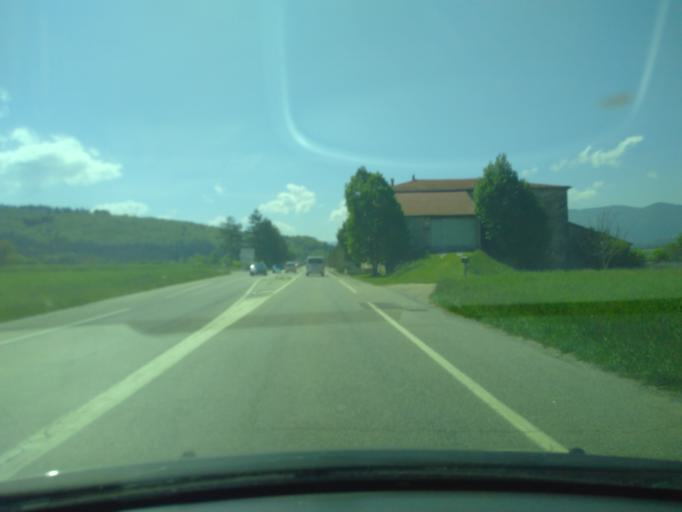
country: FR
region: Rhone-Alpes
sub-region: Departement de la Drome
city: Die
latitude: 44.7177
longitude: 5.4000
